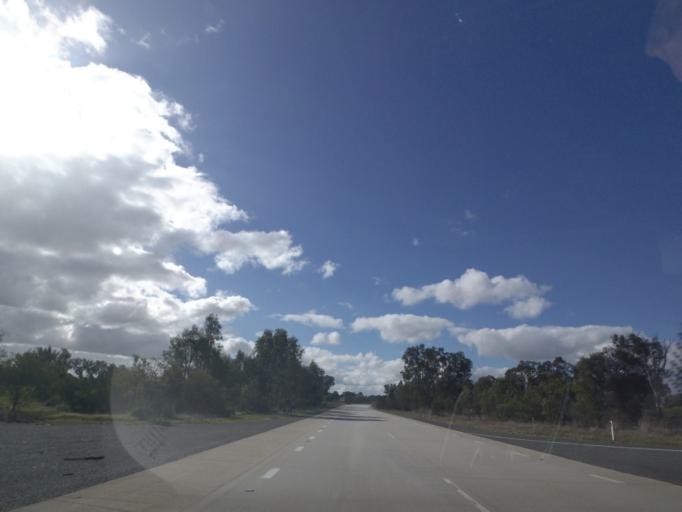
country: AU
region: New South Wales
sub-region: Greater Hume Shire
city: Holbrook
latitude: -35.8873
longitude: 147.1736
